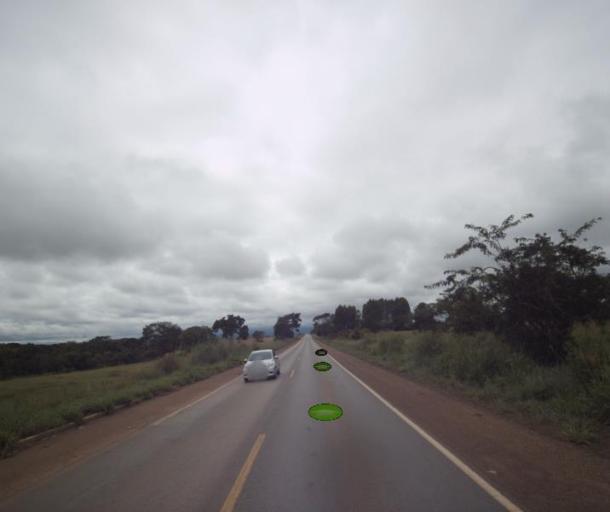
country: BR
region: Goias
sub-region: Uruacu
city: Uruacu
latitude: -14.7042
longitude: -49.1031
